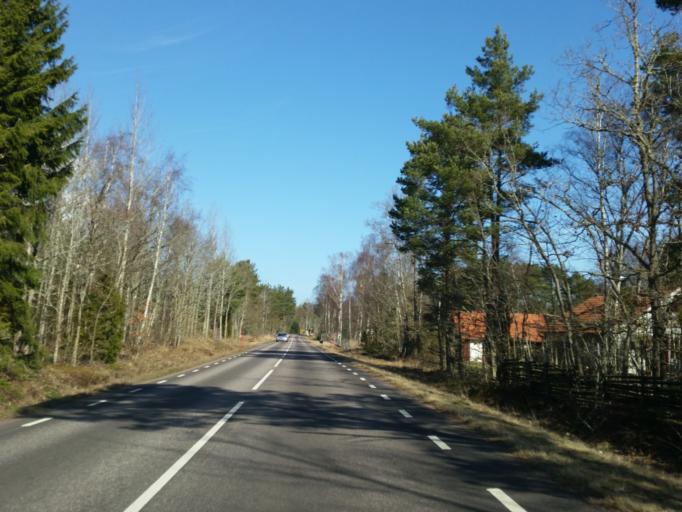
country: SE
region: Kalmar
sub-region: Monsteras Kommun
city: Timmernabben
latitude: 56.8708
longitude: 16.4298
